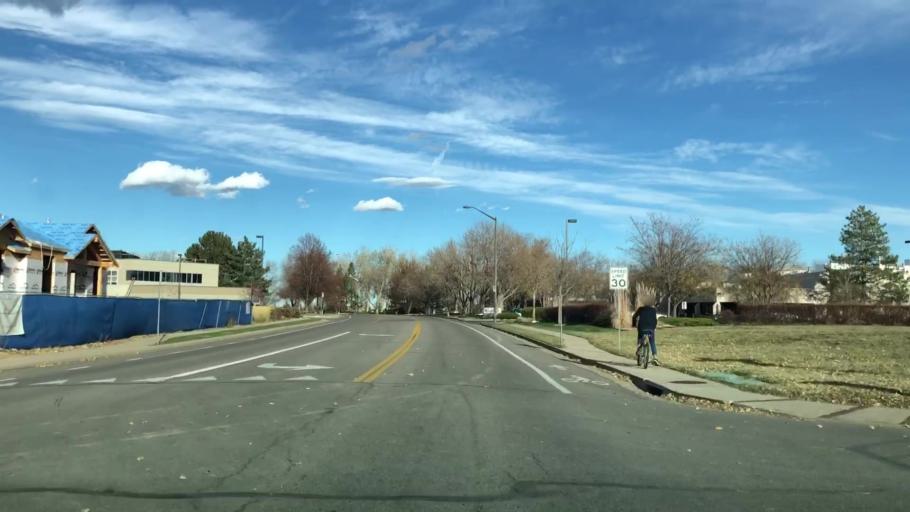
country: US
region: Colorado
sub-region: Larimer County
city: Fort Collins
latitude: 40.5560
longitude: -105.0908
